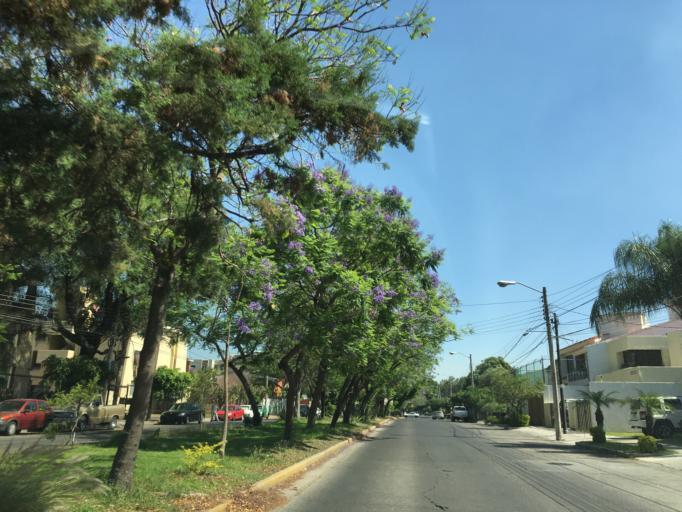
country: MX
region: Jalisco
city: Guadalajara
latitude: 20.6434
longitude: -103.3906
